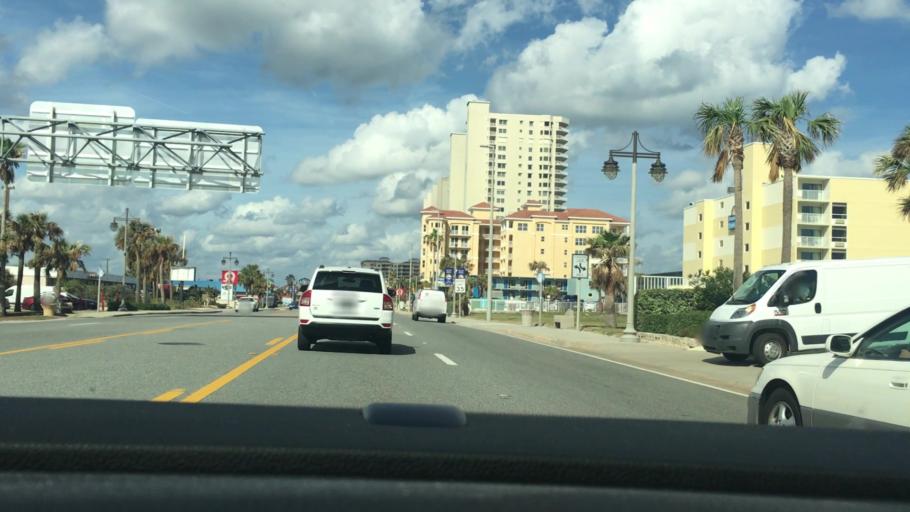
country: US
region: Florida
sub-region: Volusia County
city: Daytona Beach Shores
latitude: 29.1519
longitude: -80.9694
